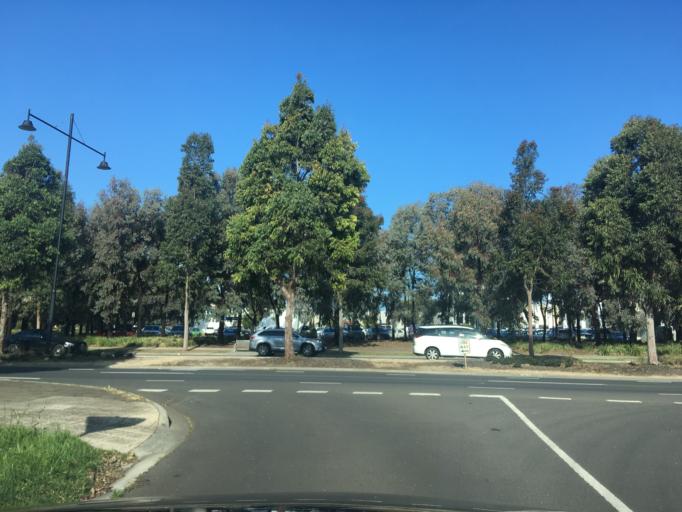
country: AU
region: Victoria
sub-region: Wyndham
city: Williams Landing
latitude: -37.8814
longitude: 144.7335
